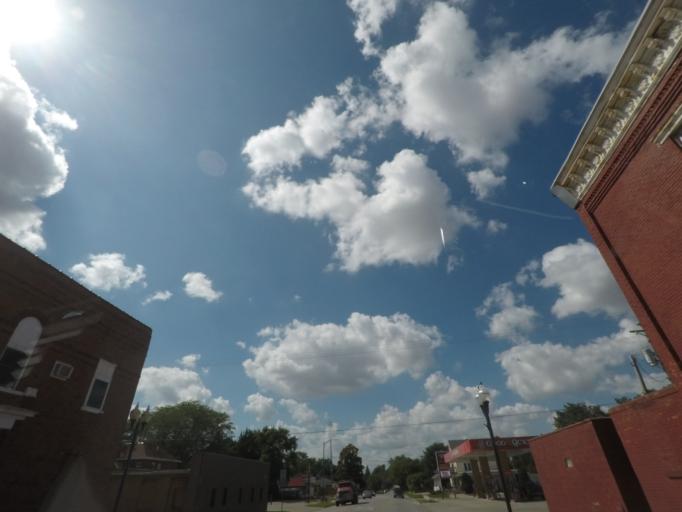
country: US
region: Iowa
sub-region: Story County
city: Nevada
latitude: 42.0228
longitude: -93.4527
